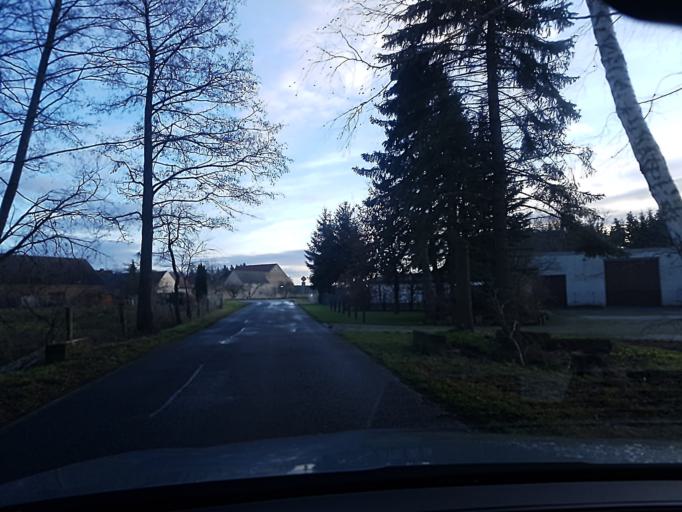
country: DE
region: Brandenburg
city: Schilda
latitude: 51.5763
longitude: 13.4058
